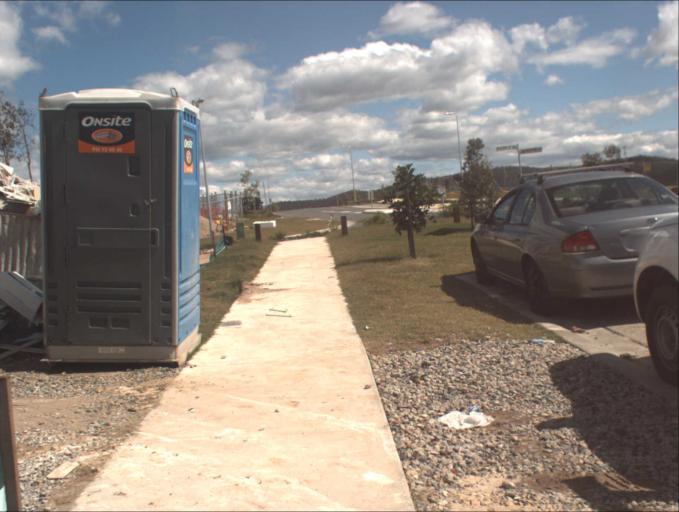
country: AU
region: Queensland
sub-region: Logan
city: Chambers Flat
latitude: -27.8028
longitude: 153.1157
